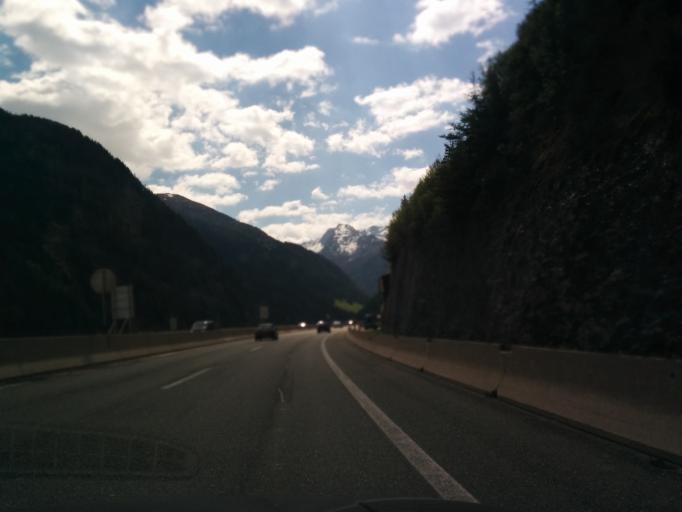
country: AT
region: Tyrol
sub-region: Politischer Bezirk Innsbruck Land
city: Gries am Brenner
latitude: 47.0344
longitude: 11.4828
